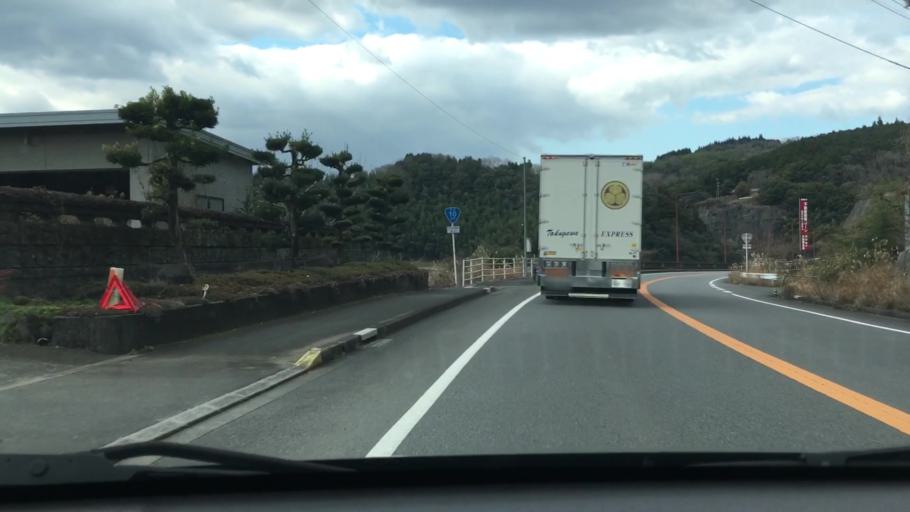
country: JP
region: Oita
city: Usuki
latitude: 33.0661
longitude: 131.6572
